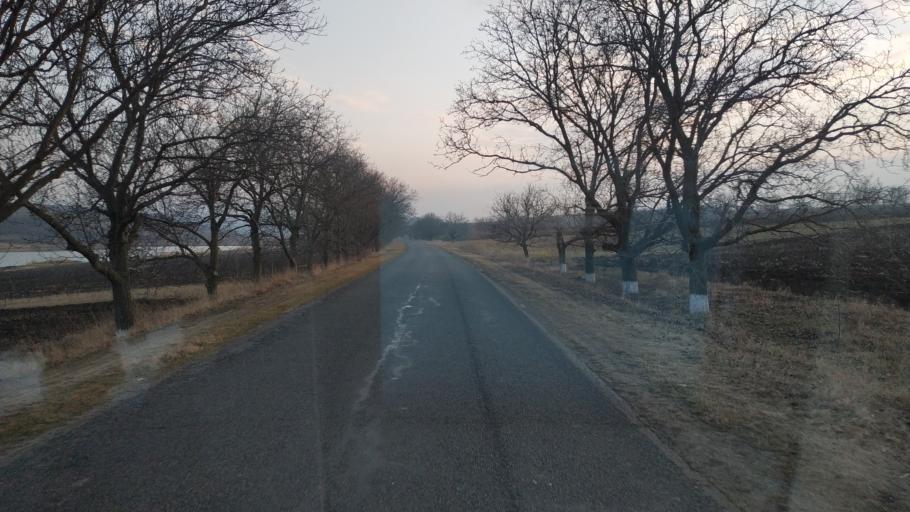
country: MD
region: Hincesti
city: Dancu
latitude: 46.6999
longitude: 28.3374
